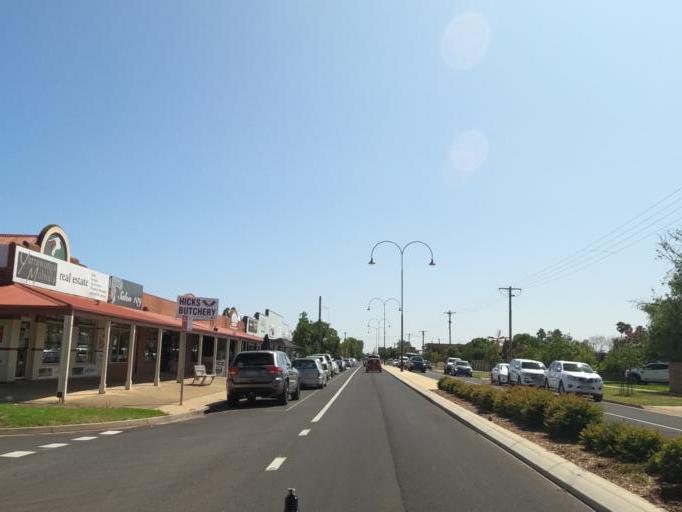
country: AU
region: New South Wales
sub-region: Corowa Shire
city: Mulwala
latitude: -35.9911
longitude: 146.0036
